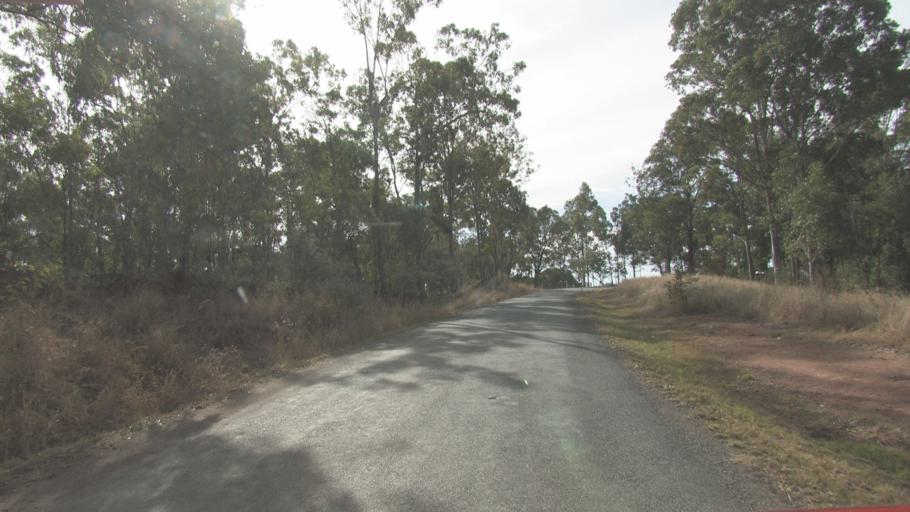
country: AU
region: Queensland
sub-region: Logan
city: Cedar Vale
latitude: -27.8978
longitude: 152.9882
